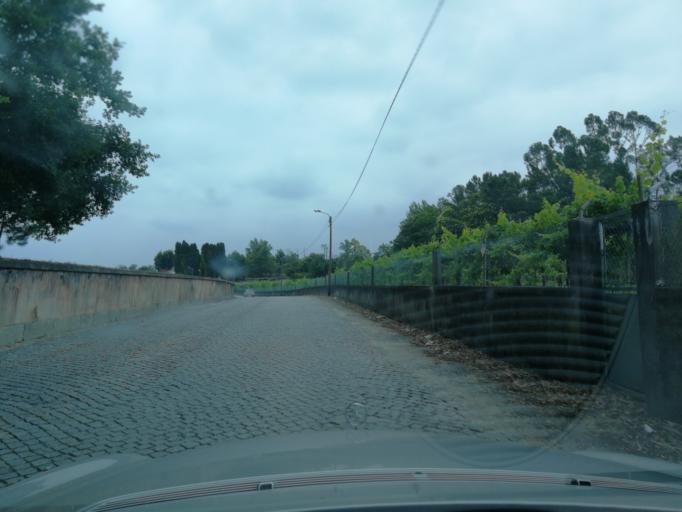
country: PT
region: Braga
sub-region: Vila Verde
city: Prado
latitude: 41.6008
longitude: -8.4416
